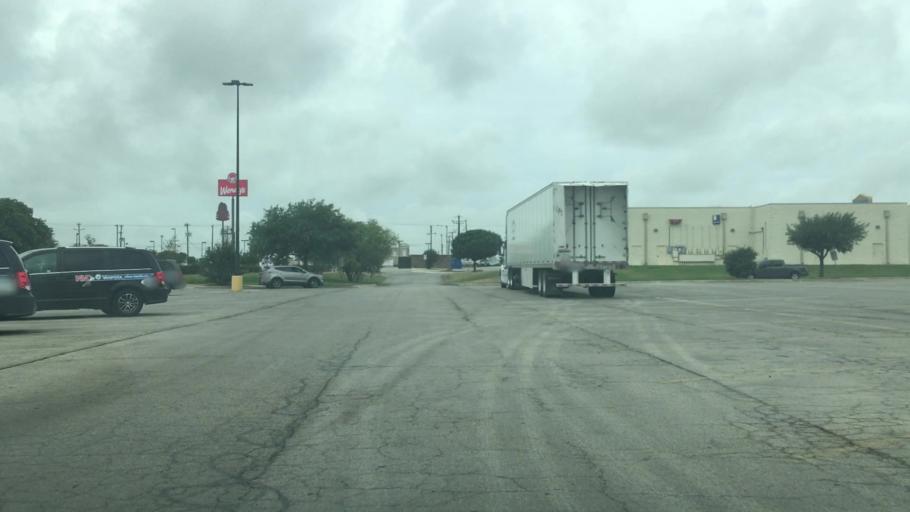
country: US
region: Texas
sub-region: Bexar County
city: Selma
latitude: 29.6026
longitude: -98.2759
